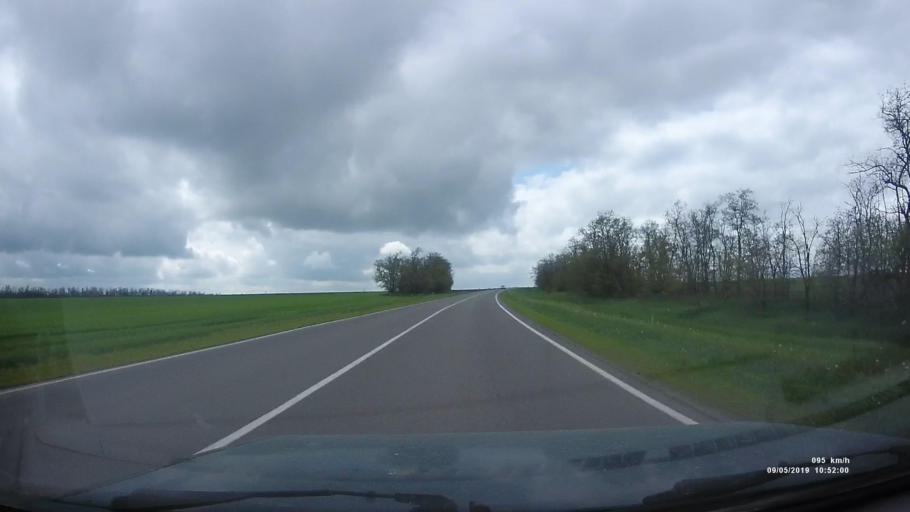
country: RU
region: Rostov
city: Peshkovo
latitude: 46.9072
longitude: 39.3549
